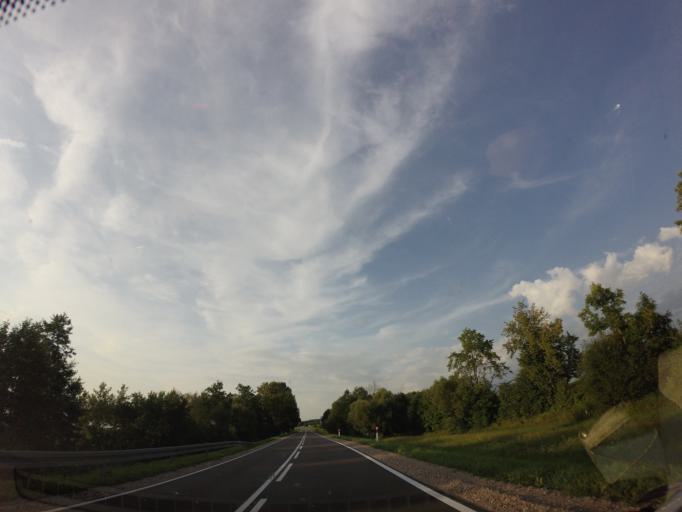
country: LT
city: Lazdijai
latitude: 54.1346
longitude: 23.4642
